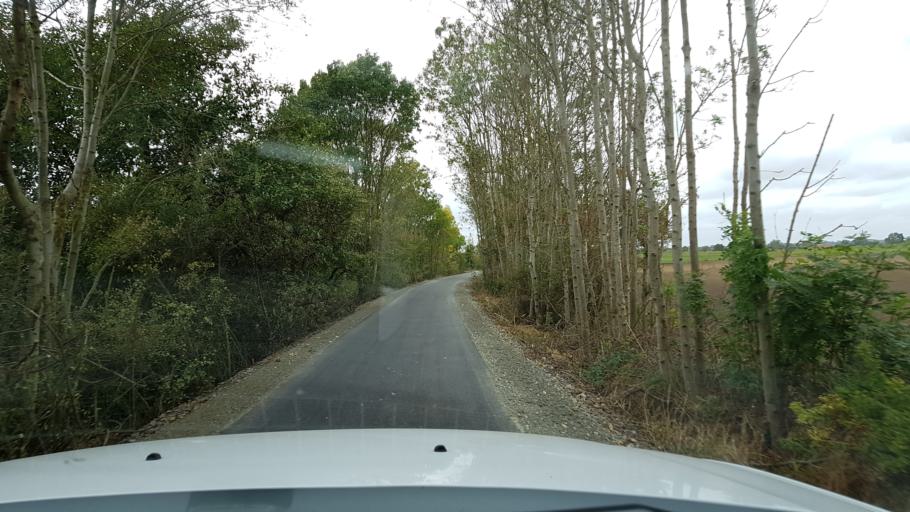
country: PL
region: West Pomeranian Voivodeship
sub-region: Powiat gryfinski
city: Moryn
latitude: 52.8642
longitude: 14.3576
